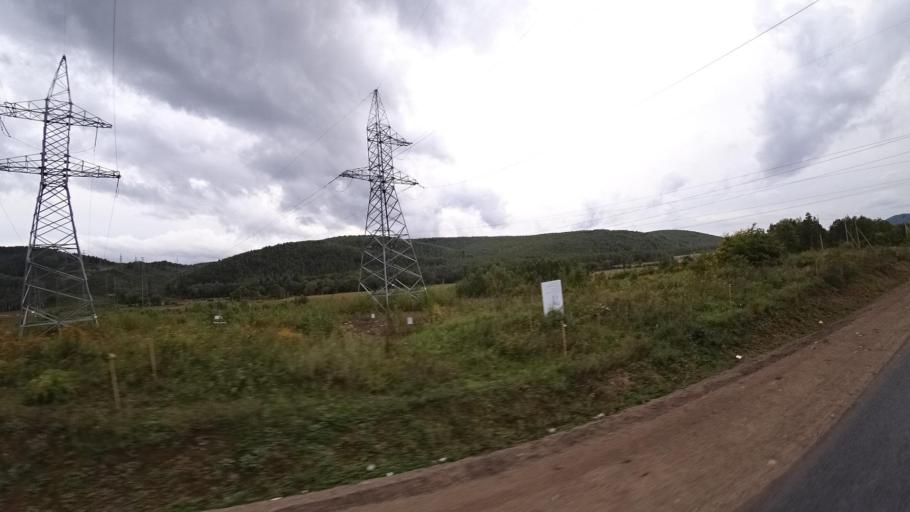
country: RU
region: Jewish Autonomous Oblast
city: Khingansk
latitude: 48.9904
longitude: 131.0939
